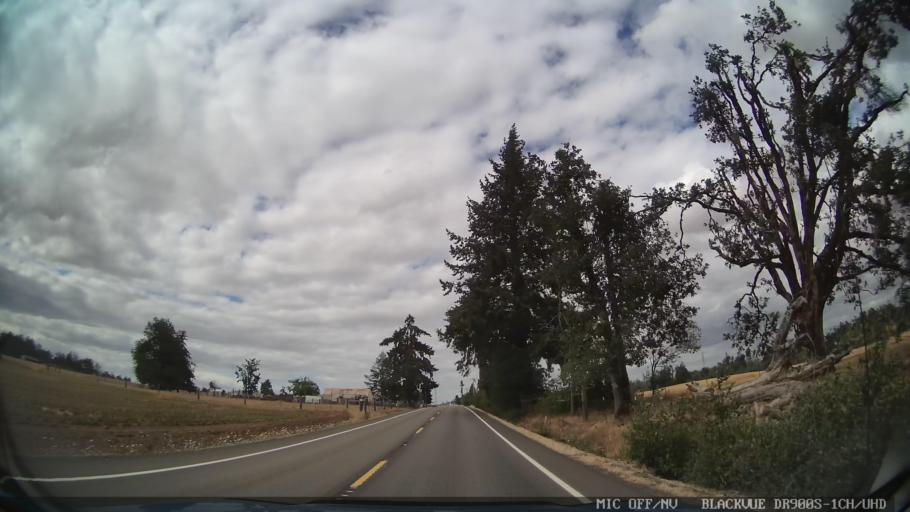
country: US
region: Oregon
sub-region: Marion County
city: Sublimity
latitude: 44.8578
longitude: -122.7929
